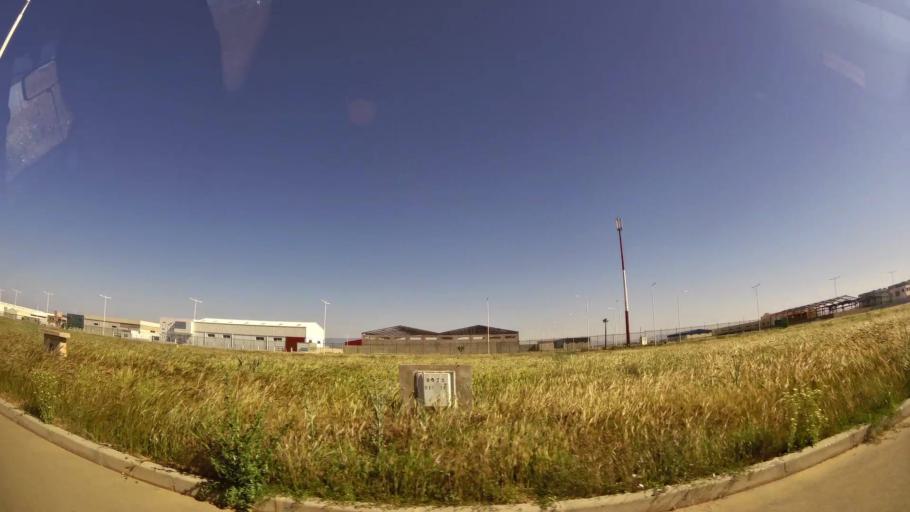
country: MA
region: Oriental
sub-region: Oujda-Angad
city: Oujda
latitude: 34.7723
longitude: -1.9343
